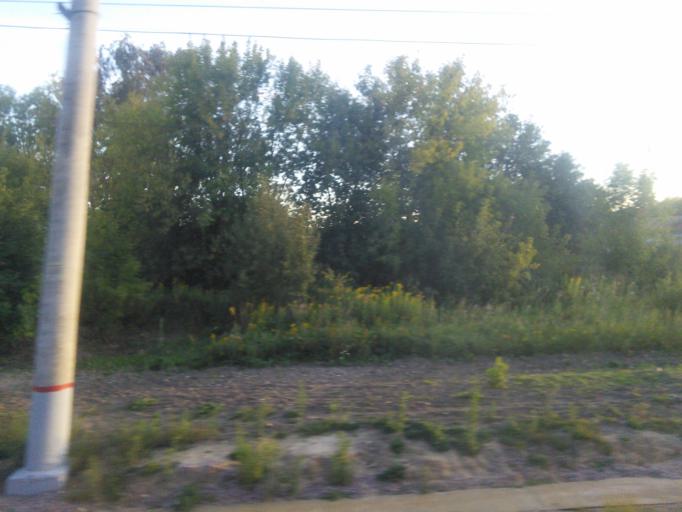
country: RU
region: Moskovskaya
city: Elektrougli
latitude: 55.7326
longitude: 38.1929
